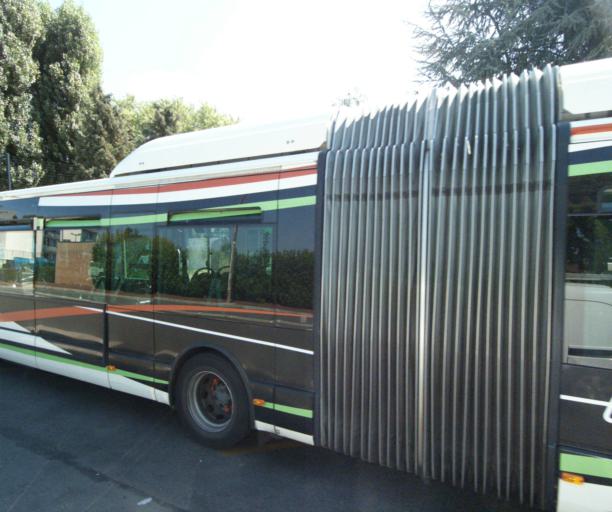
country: FR
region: Nord-Pas-de-Calais
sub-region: Departement du Nord
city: Halluin
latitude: 50.7794
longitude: 3.1118
